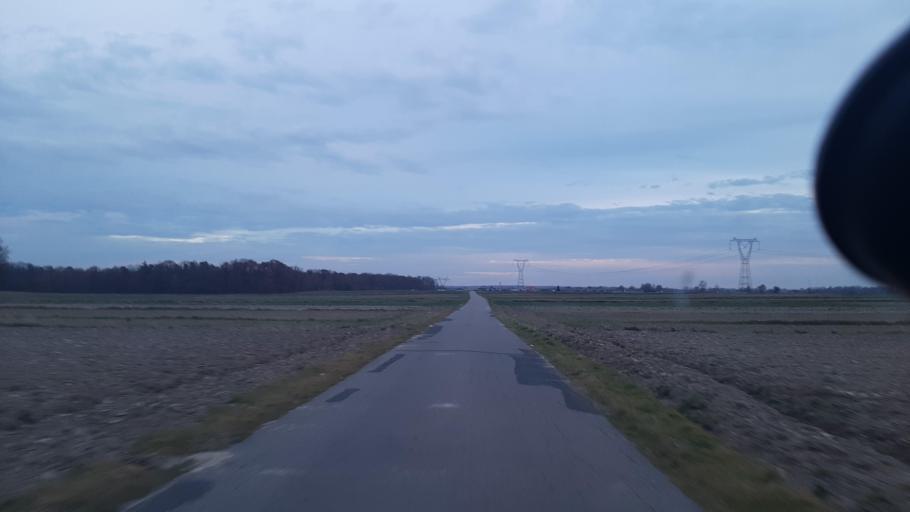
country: PL
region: Lublin Voivodeship
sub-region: Powiat lubelski
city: Garbow
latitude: 51.3753
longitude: 22.3732
